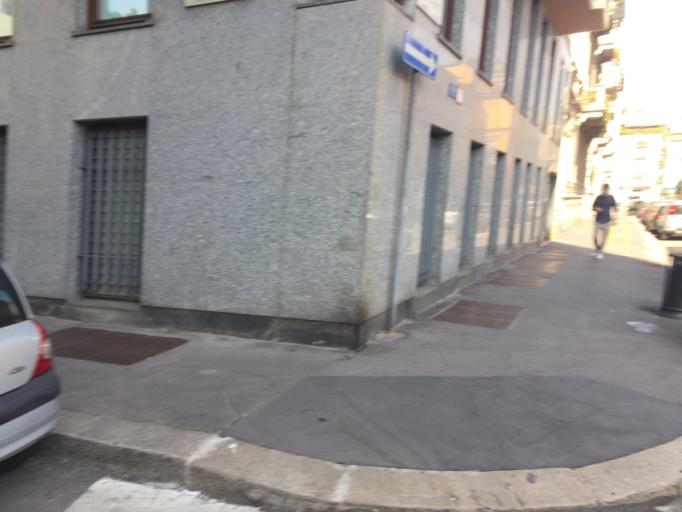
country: IT
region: Lombardy
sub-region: Citta metropolitana di Milano
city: Milano
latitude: 45.4690
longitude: 9.2022
